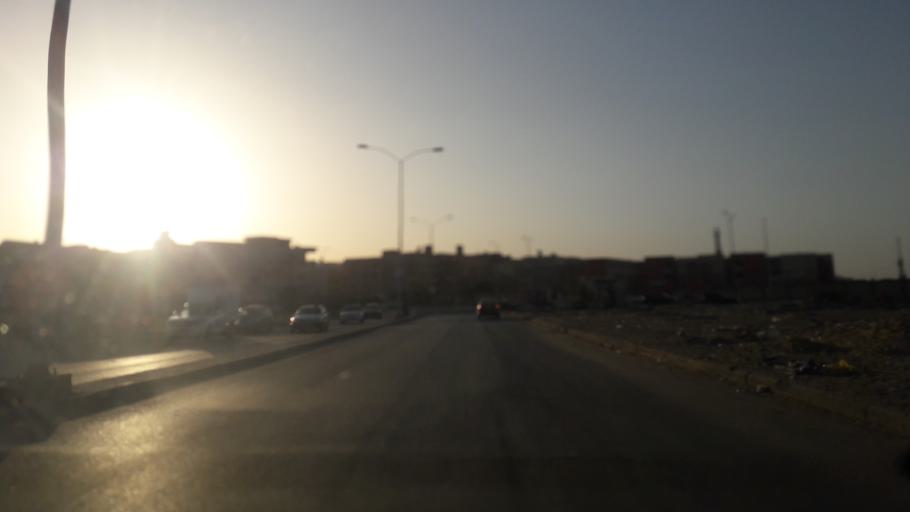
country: EG
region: Al Jizah
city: Madinat Sittah Uktubar
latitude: 29.9491
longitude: 30.9398
